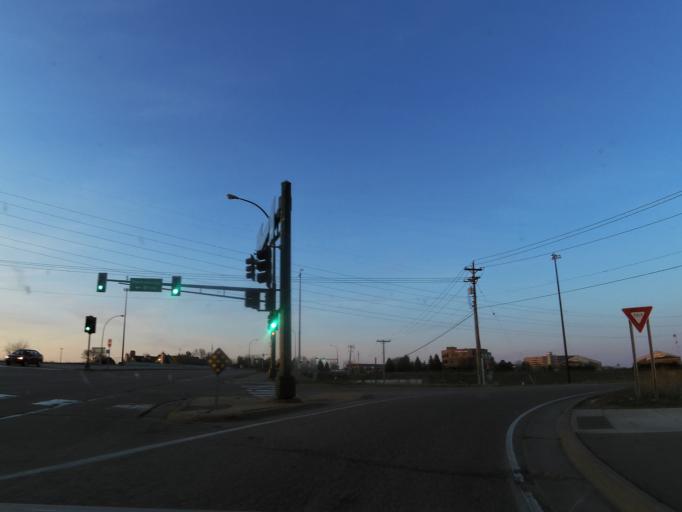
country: US
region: Minnesota
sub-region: Hennepin County
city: Eden Prairie
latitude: 44.8614
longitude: -93.4255
